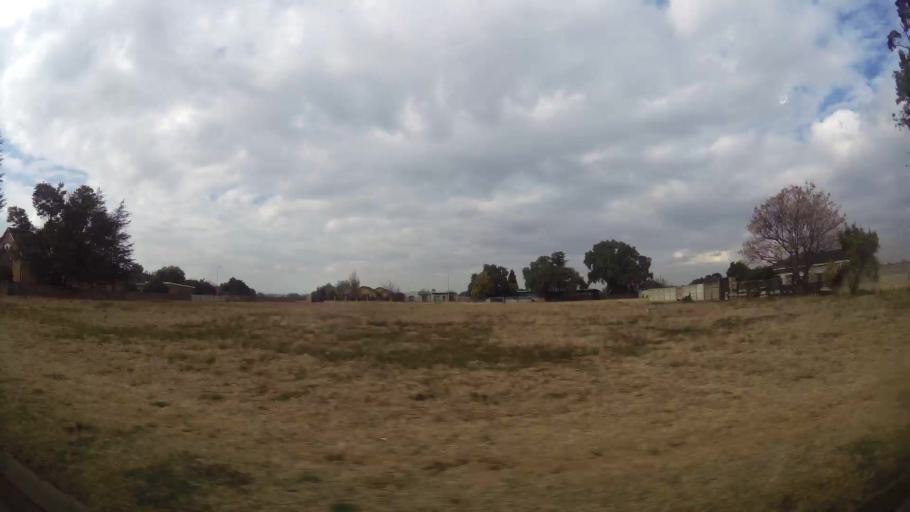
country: ZA
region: Gauteng
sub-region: Sedibeng District Municipality
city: Meyerton
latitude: -26.5919
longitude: 27.9981
